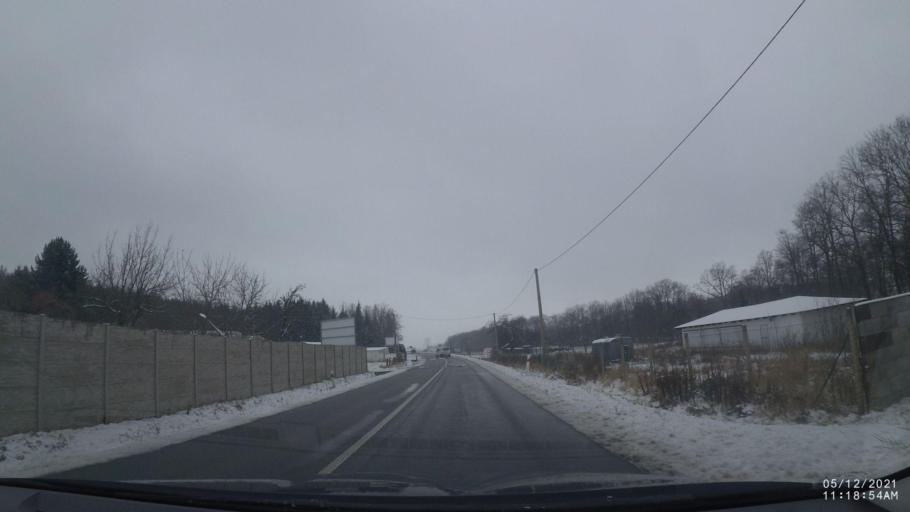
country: CZ
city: Solnice
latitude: 50.1950
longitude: 16.2306
